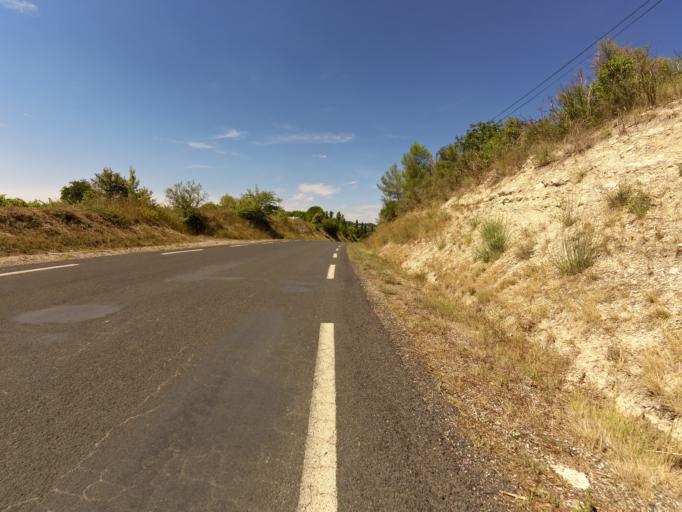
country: FR
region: Languedoc-Roussillon
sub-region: Departement de l'Herault
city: Boisseron
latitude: 43.7679
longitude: 4.0935
